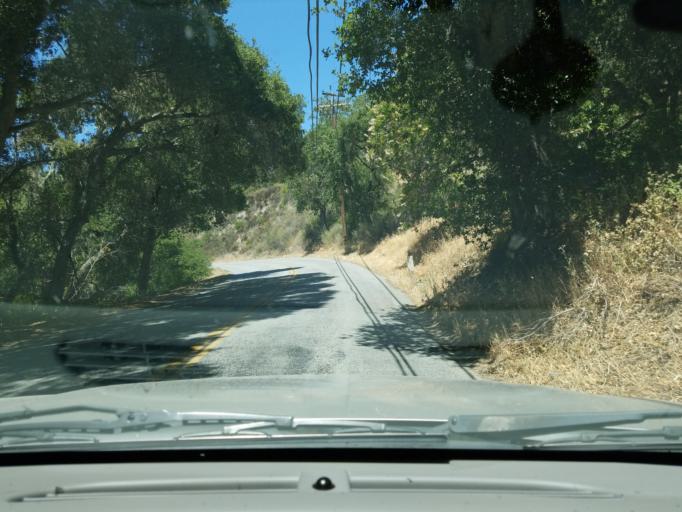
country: US
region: California
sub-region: Monterey County
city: Carmel Valley Village
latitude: 36.4546
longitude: -121.6993
